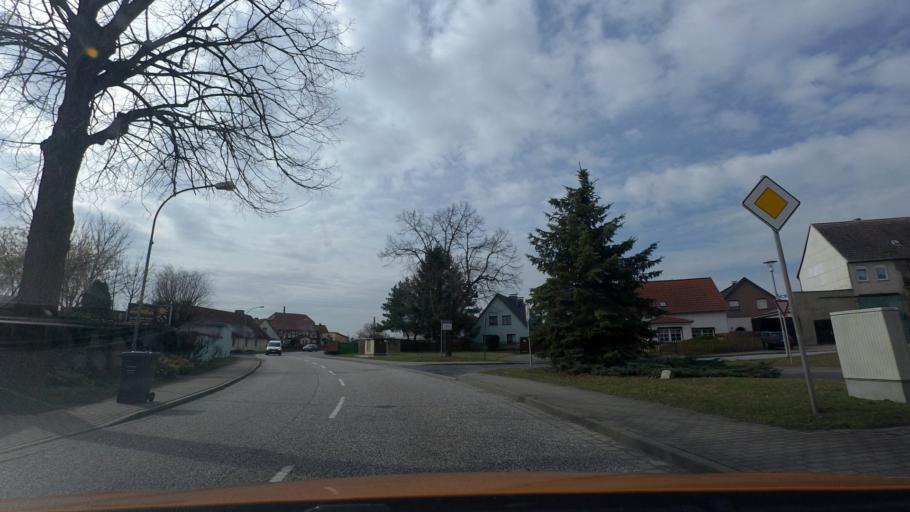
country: DE
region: Saxony-Anhalt
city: Erxleben
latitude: 52.2196
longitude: 11.2346
